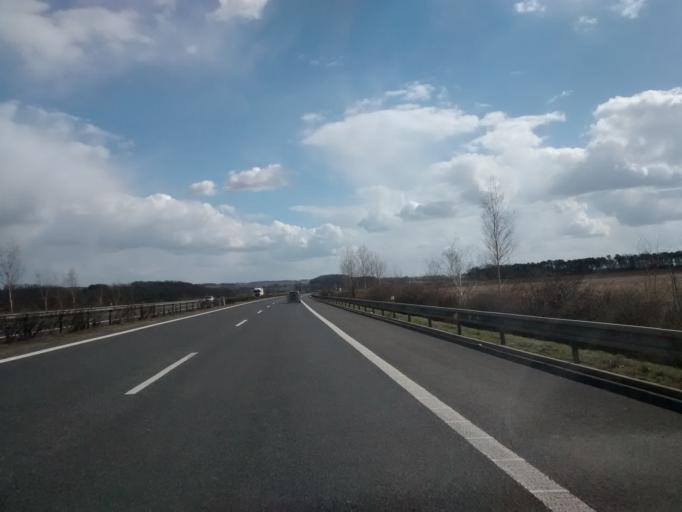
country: CZ
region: Ustecky
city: Roudnice nad Labem
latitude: 50.3860
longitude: 14.2389
